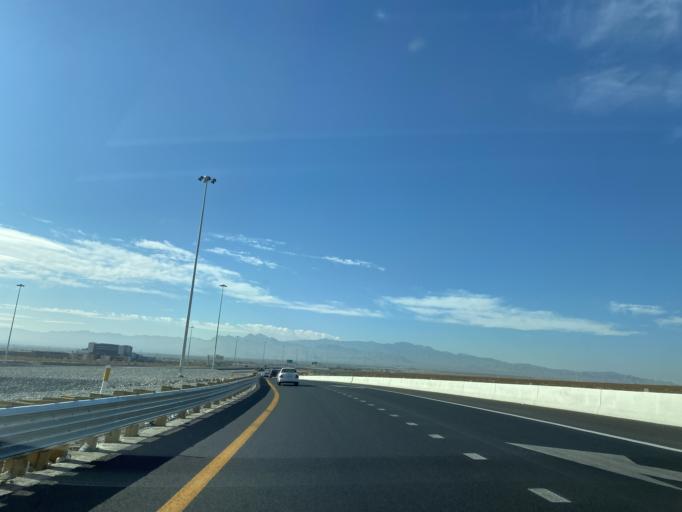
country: US
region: Nevada
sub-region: Clark County
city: Nellis Air Force Base
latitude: 36.2907
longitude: -115.0816
